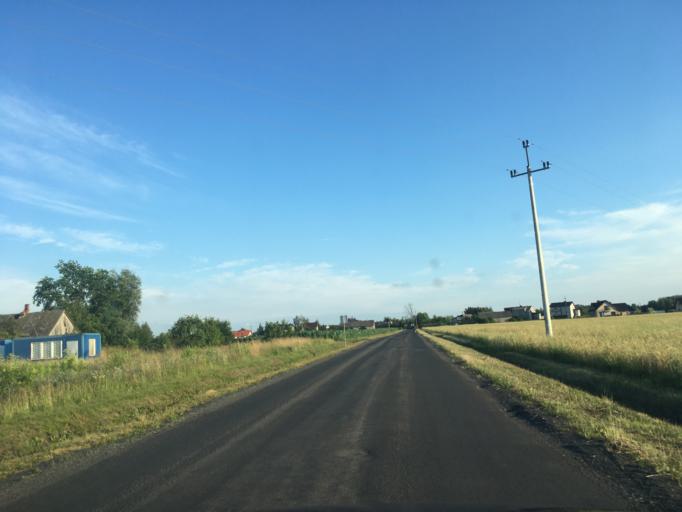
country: PL
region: Masovian Voivodeship
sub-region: Powiat grodziski
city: Grodzisk Mazowiecki
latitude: 52.1211
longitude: 20.5809
